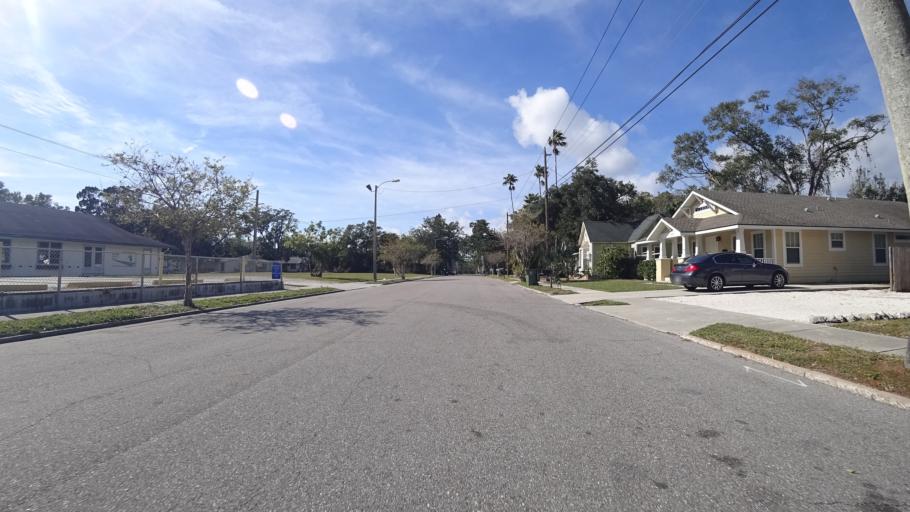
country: US
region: Florida
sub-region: Manatee County
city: Bradenton
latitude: 27.4923
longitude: -82.5765
